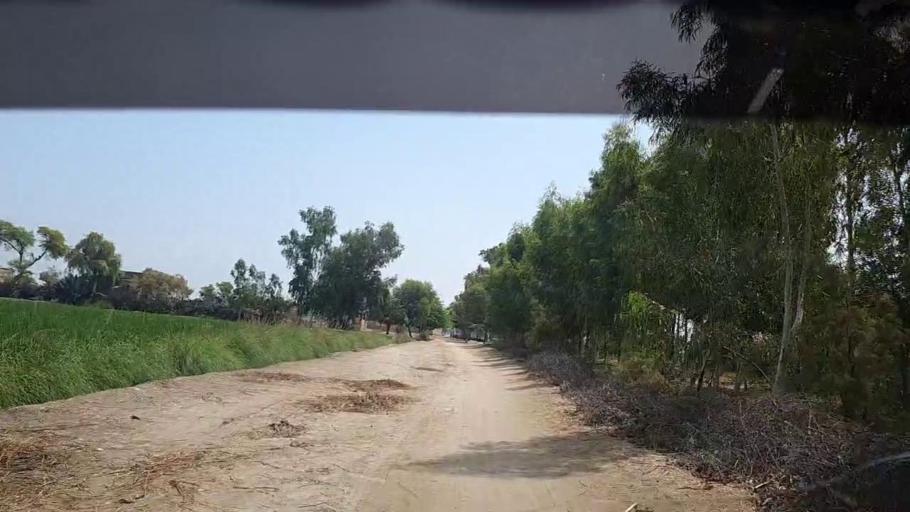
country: PK
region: Sindh
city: Tangwani
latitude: 28.2288
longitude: 68.8998
